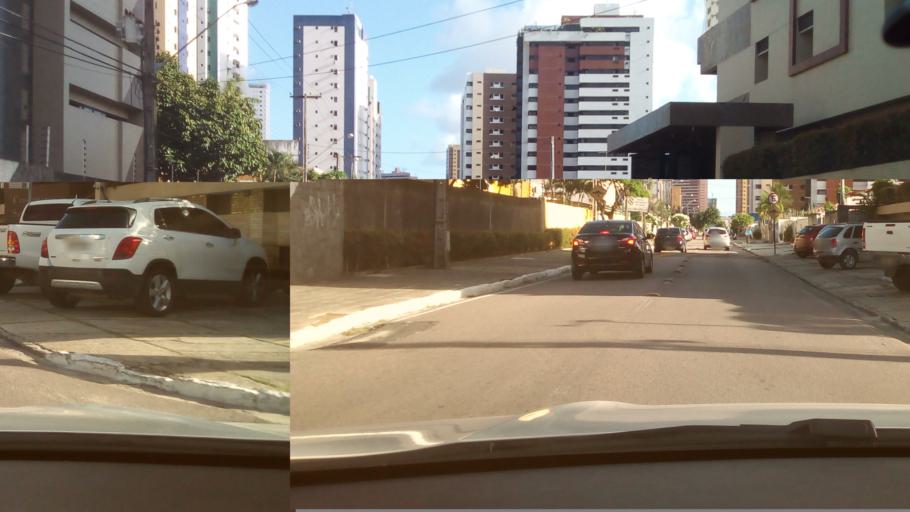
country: BR
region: Paraiba
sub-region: Joao Pessoa
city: Joao Pessoa
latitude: -7.1049
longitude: -34.8384
